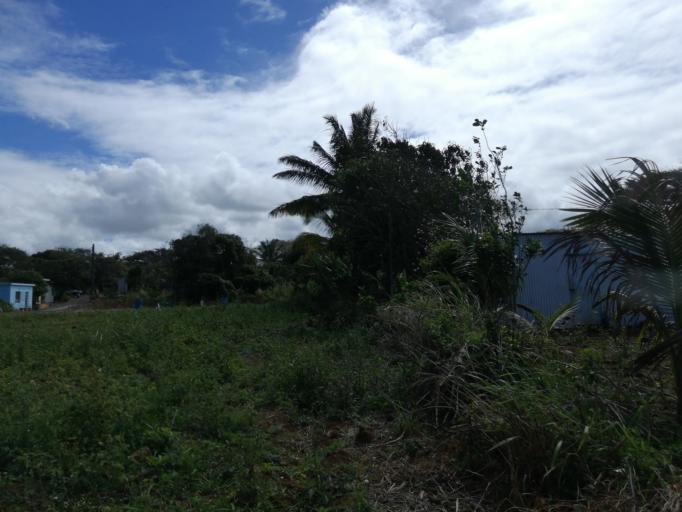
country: MU
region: Grand Port
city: Plaine Magnien
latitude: -20.4652
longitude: 57.6763
